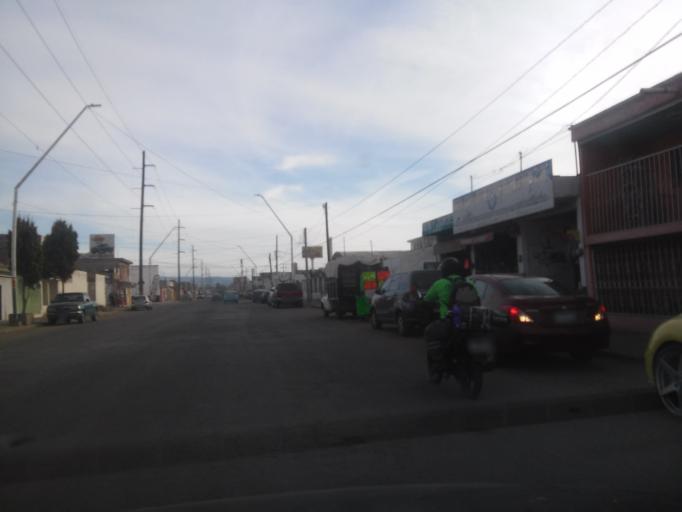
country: MX
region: Durango
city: Victoria de Durango
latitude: 24.0169
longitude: -104.6327
